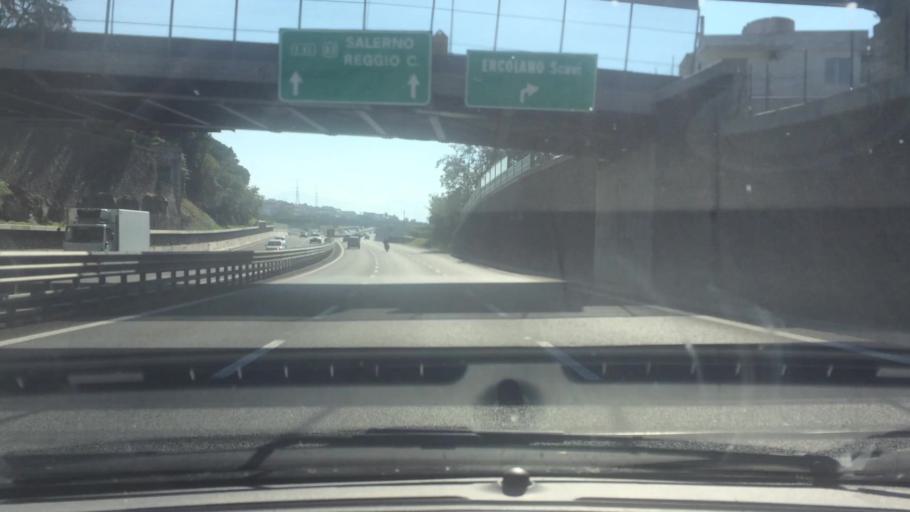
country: IT
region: Campania
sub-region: Provincia di Napoli
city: Ercolano
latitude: 40.8137
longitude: 14.3576
